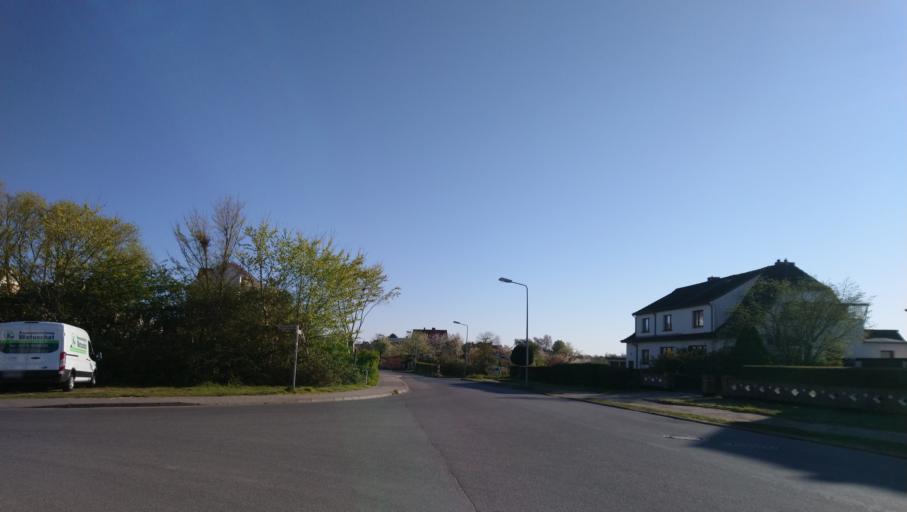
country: DE
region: Mecklenburg-Vorpommern
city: Rostock
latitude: 54.0647
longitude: 12.1311
